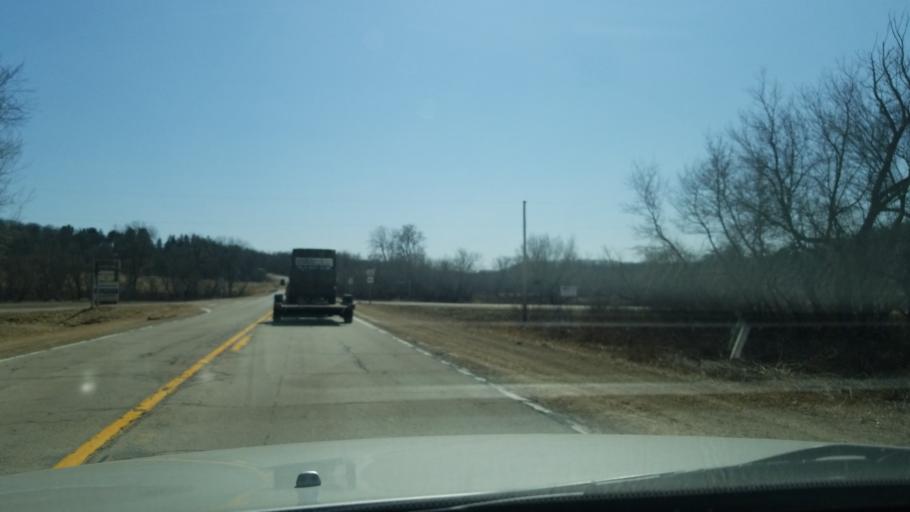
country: US
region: Wisconsin
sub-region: Iowa County
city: Mineral Point
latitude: 42.8692
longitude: -90.2047
